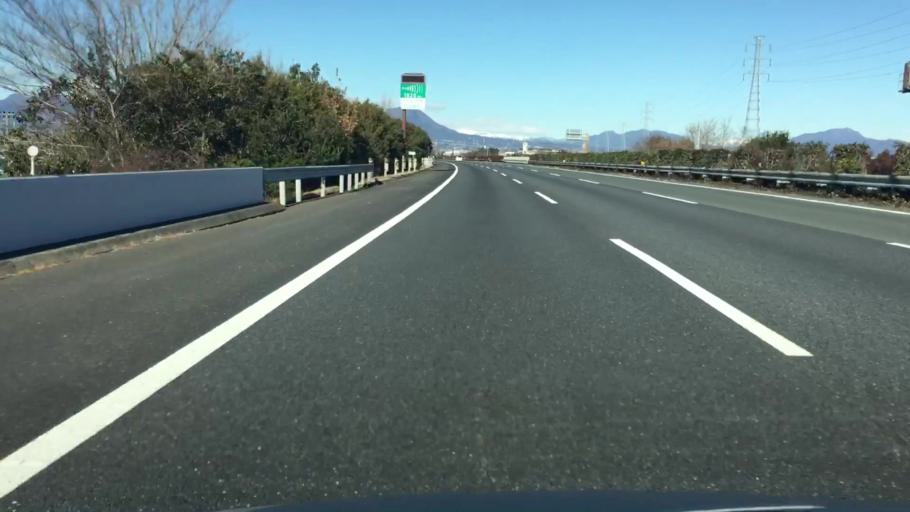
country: JP
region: Gunma
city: Takasaki
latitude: 36.3418
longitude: 139.0561
